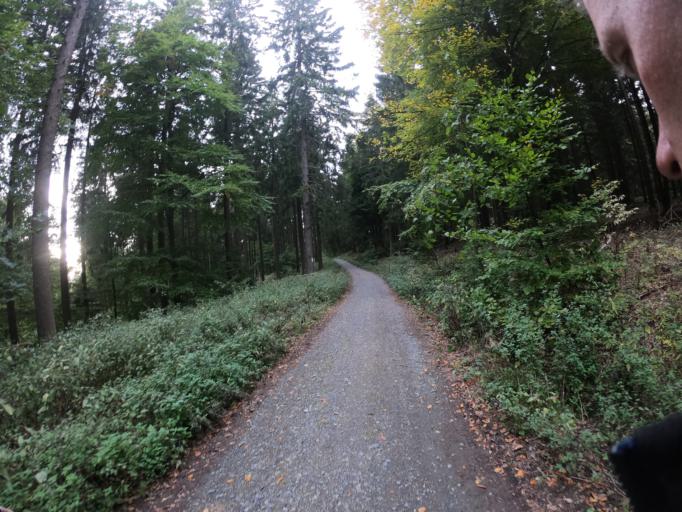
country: DE
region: Hesse
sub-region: Regierungsbezirk Darmstadt
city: Glashutten
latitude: 50.2290
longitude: 8.4322
